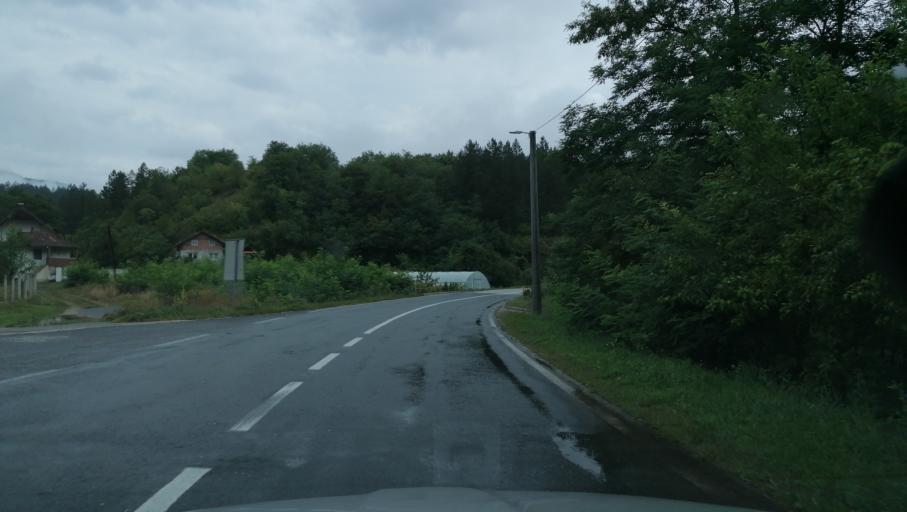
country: RS
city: Durici
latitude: 43.7497
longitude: 19.4005
